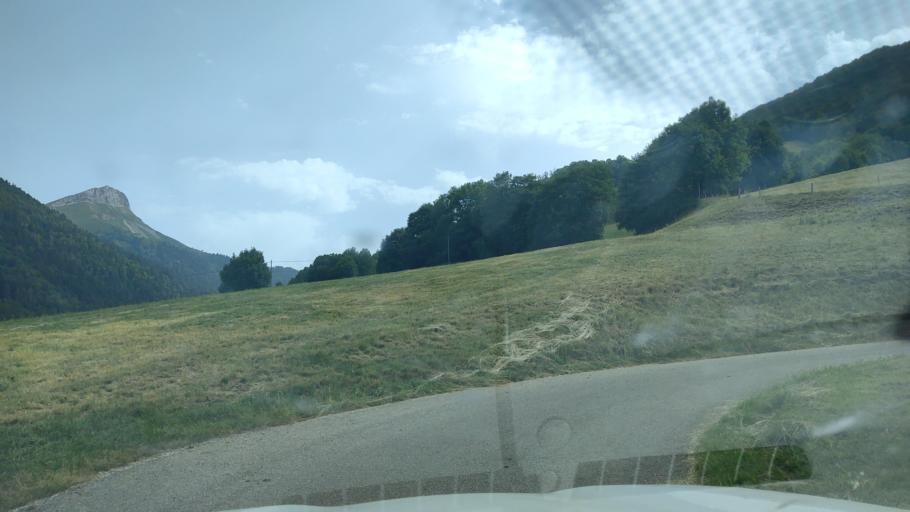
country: FR
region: Rhone-Alpes
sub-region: Departement de la Savoie
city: Cruet
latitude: 45.6096
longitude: 6.1123
